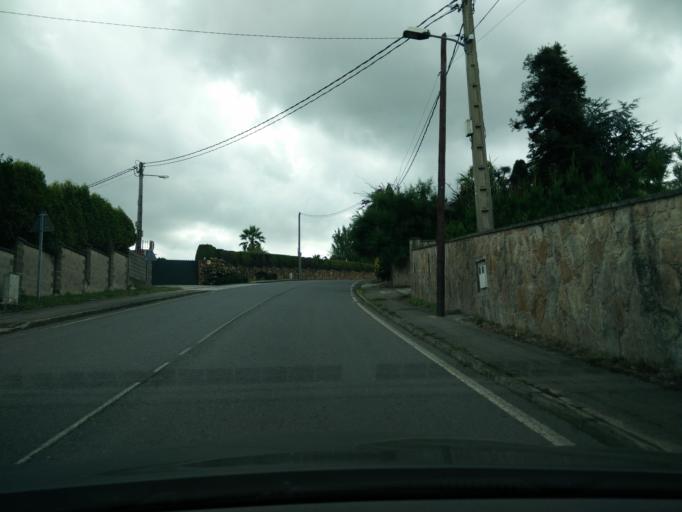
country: ES
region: Galicia
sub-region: Provincia da Coruna
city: Culleredo
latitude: 43.3272
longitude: -8.4034
